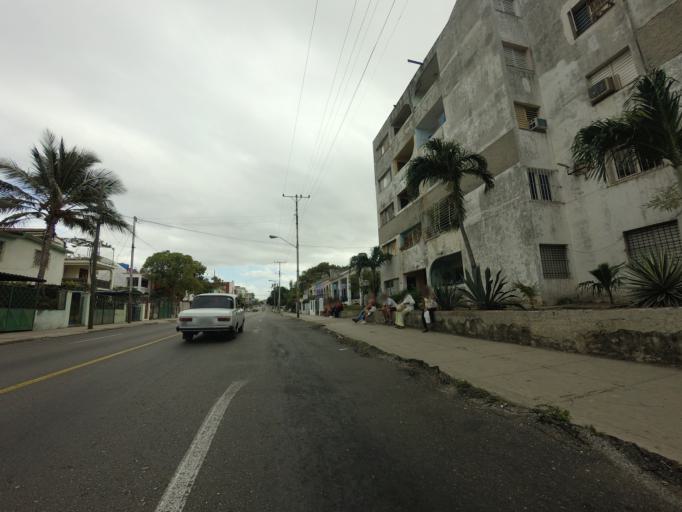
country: CU
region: La Habana
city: Havana
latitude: 23.1312
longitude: -82.4033
